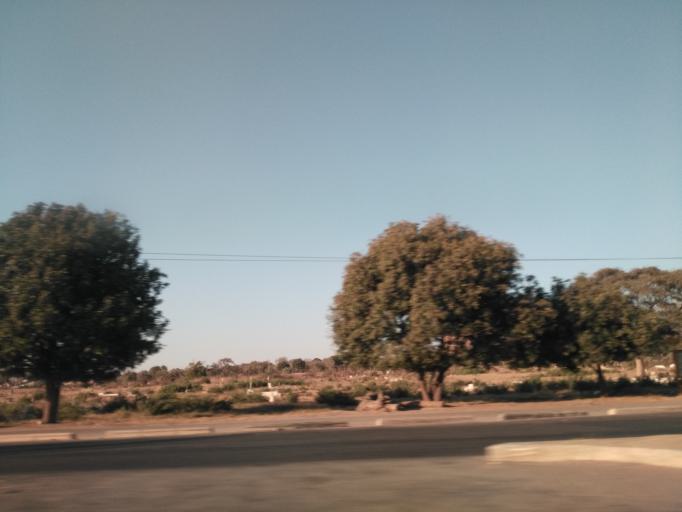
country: TZ
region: Dodoma
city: Dodoma
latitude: -6.1740
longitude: 35.7362
